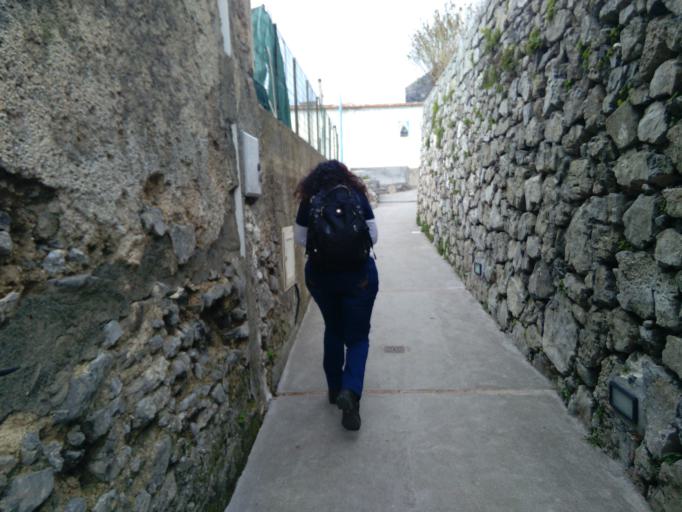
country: IT
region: Campania
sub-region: Provincia di Salerno
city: Positano
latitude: 40.6292
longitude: 14.5028
